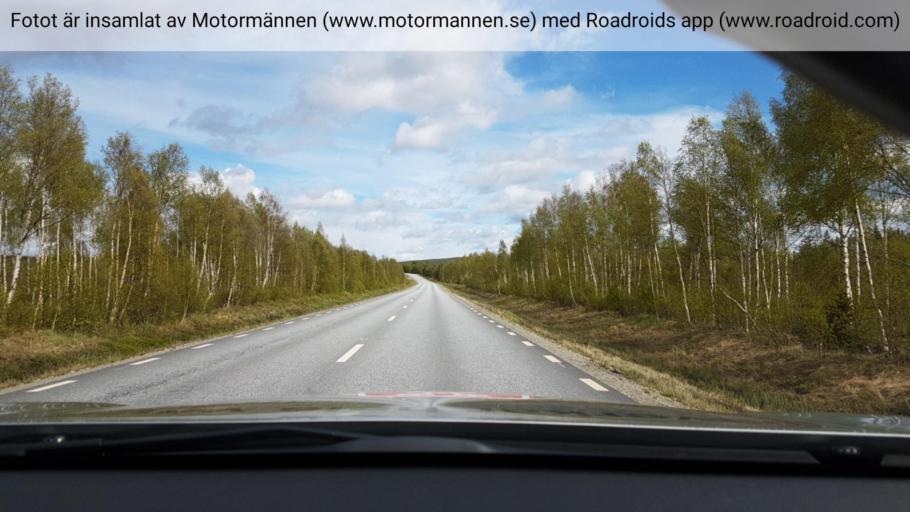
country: SE
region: Vaesterbotten
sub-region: Asele Kommun
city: Insjon
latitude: 64.1979
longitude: 17.5624
